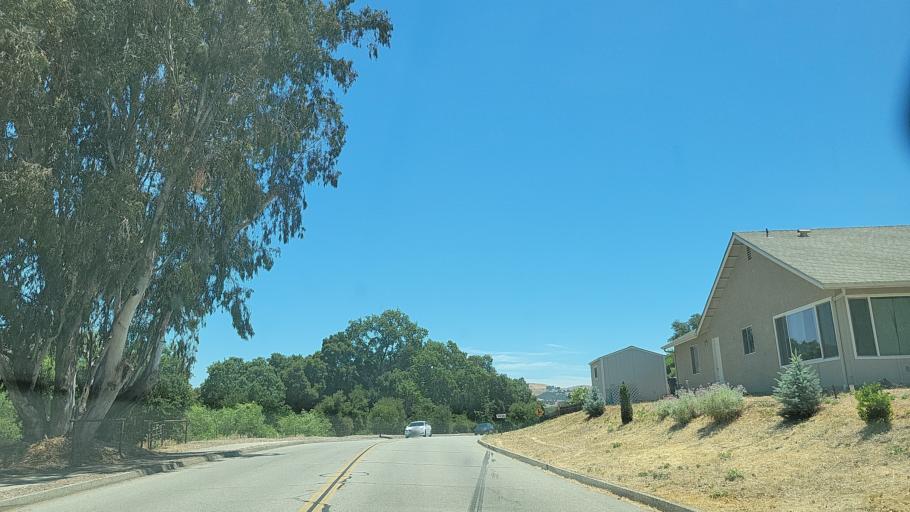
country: US
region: California
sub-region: San Luis Obispo County
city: Atascadero
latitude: 35.5122
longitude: -120.6743
